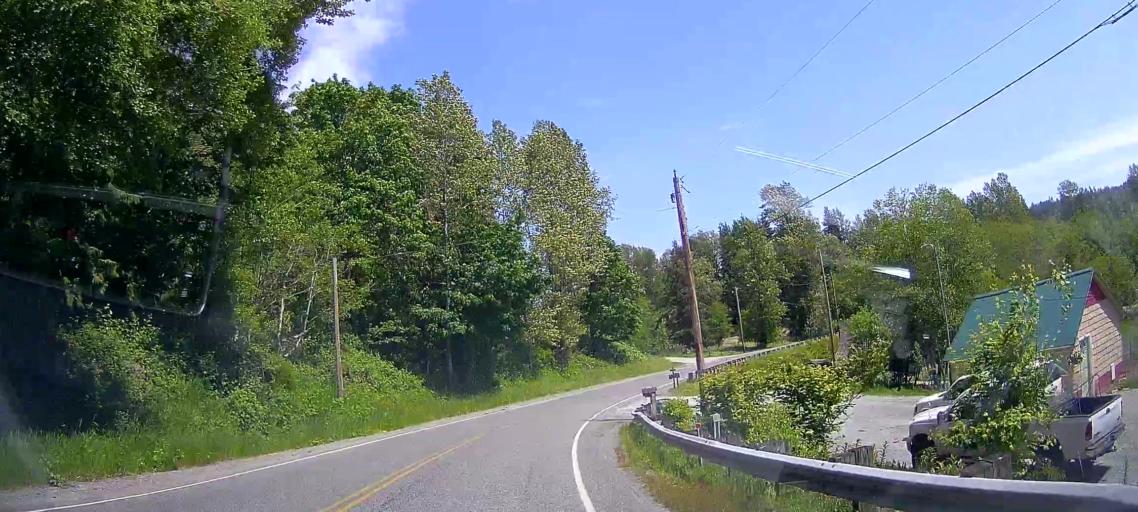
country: US
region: Washington
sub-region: Skagit County
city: Big Lake
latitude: 48.3964
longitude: -122.2876
